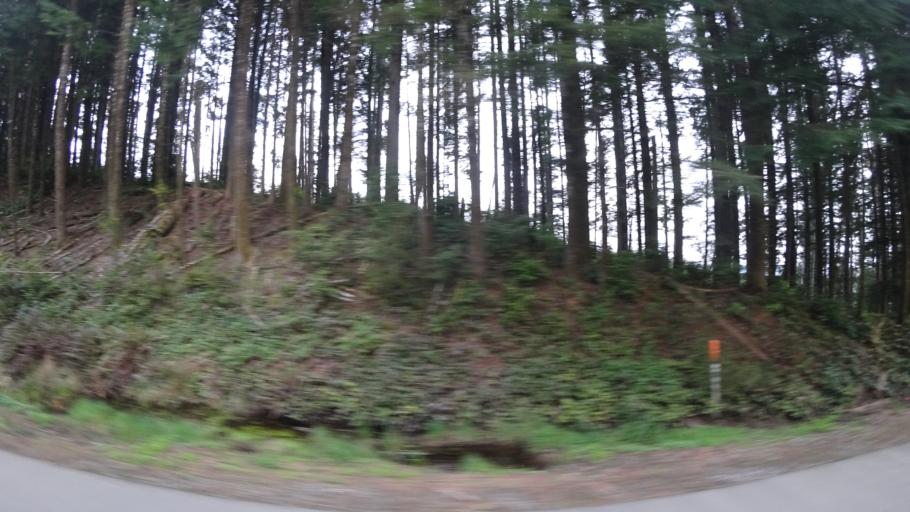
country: US
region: Oregon
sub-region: Coos County
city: Barview
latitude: 43.2442
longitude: -124.2878
